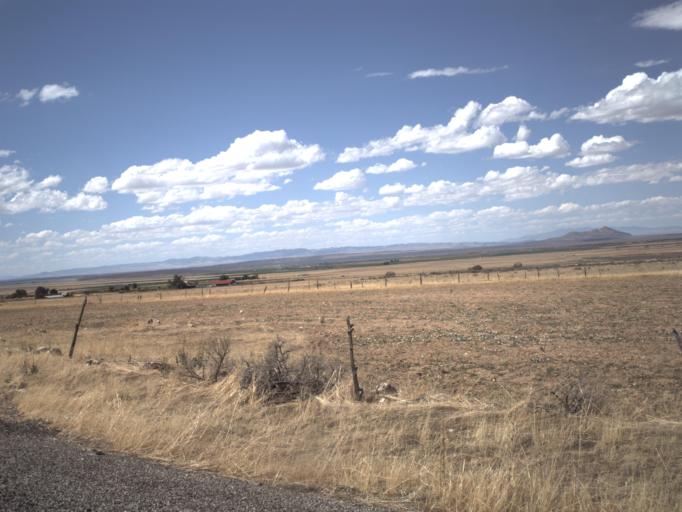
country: US
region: Utah
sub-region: Millard County
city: Fillmore
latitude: 39.1149
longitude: -112.2636
